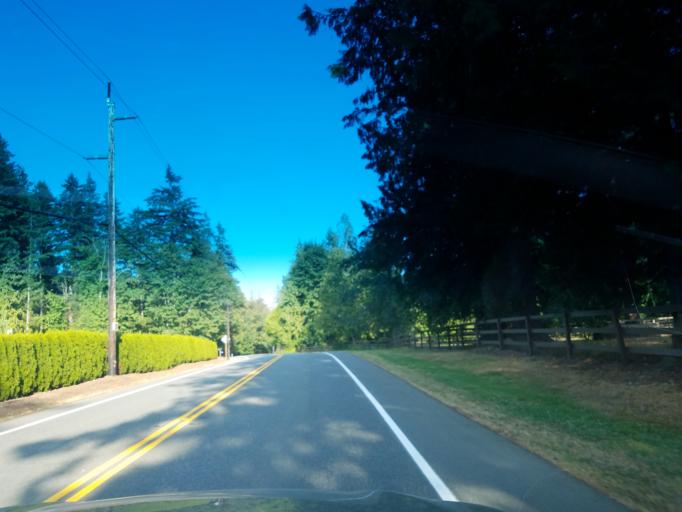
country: US
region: Washington
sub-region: King County
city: Union Hill-Novelty Hill
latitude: 47.6623
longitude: -122.0151
